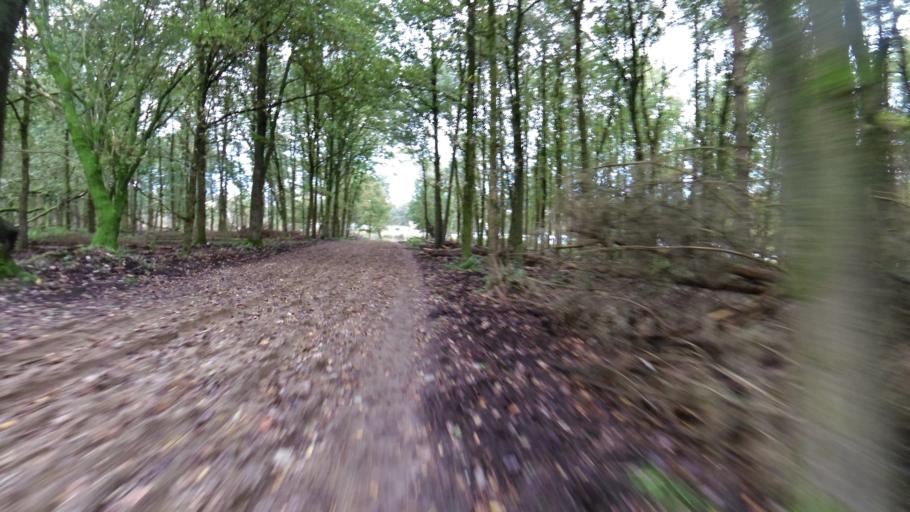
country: NL
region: Gelderland
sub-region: Gemeente Renkum
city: Wolfheze
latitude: 52.0245
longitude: 5.8090
